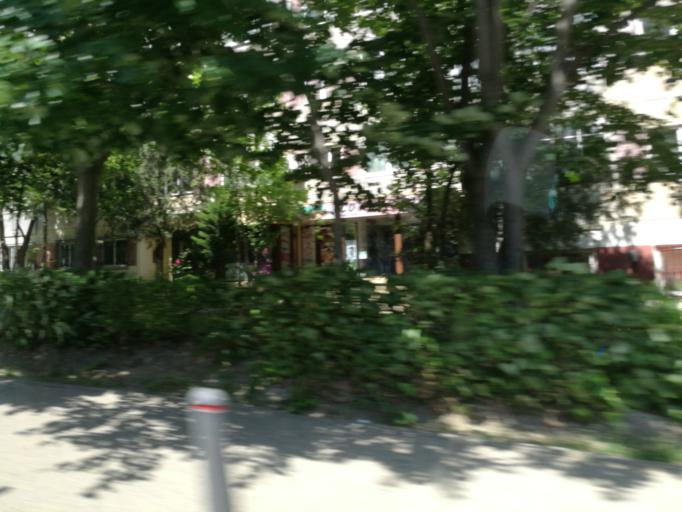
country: RO
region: Constanta
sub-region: Municipiul Constanta
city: Constanta
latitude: 44.2036
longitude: 28.6264
